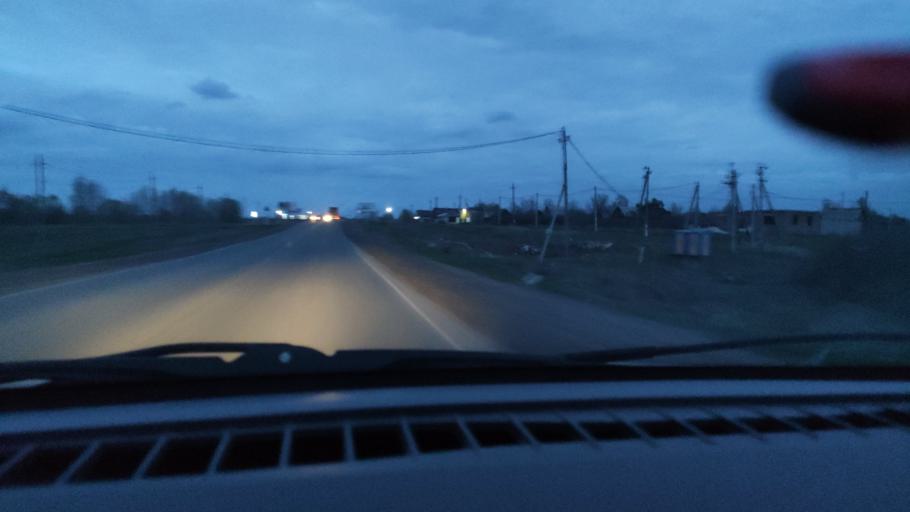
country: RU
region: Orenburg
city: Tatarskaya Kargala
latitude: 51.9008
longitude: 55.1666
